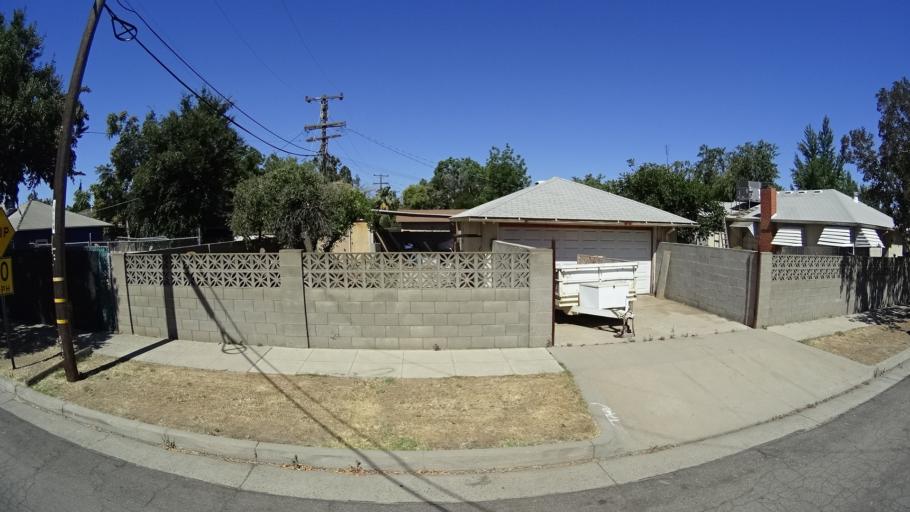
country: US
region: California
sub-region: Fresno County
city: Fresno
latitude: 36.7835
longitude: -119.8198
